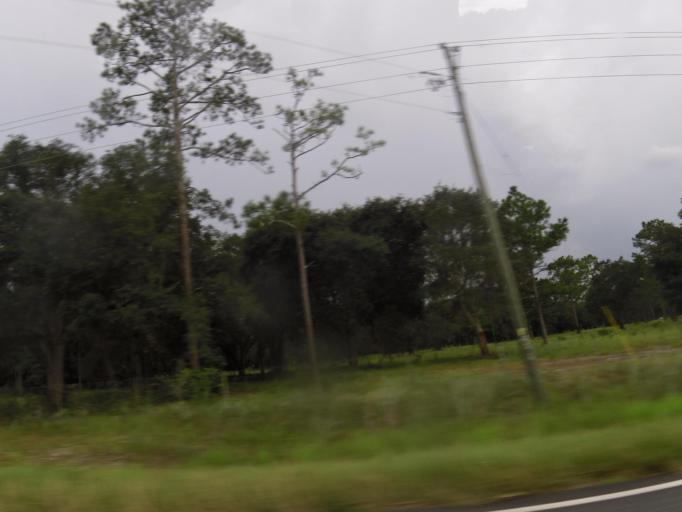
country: US
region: Florida
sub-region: Baker County
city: Macclenny
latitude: 30.3947
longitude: -82.1815
